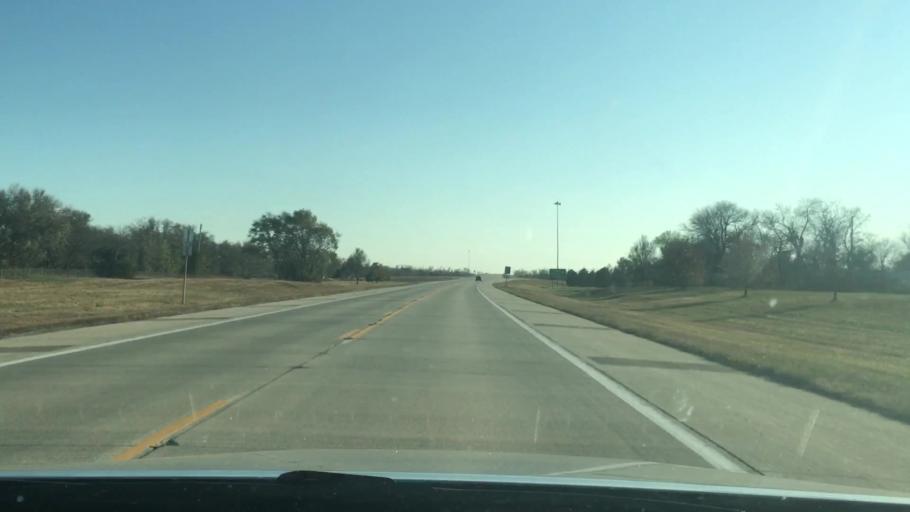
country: US
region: Kansas
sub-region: Reno County
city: Hutchinson
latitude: 38.0642
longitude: -97.9860
